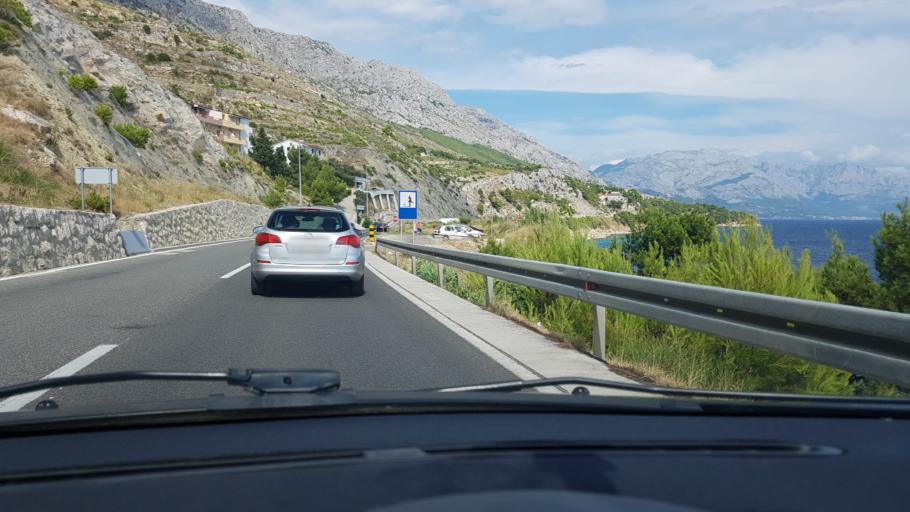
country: HR
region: Splitsko-Dalmatinska
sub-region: Grad Omis
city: Omis
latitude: 43.4089
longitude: 16.7585
